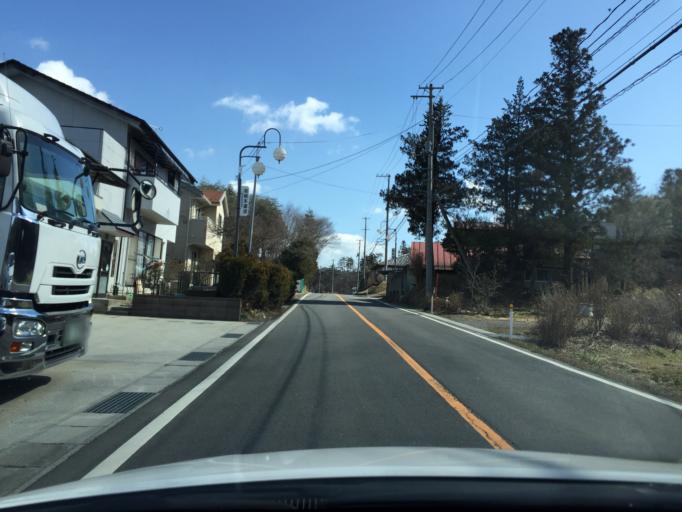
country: JP
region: Fukushima
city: Funehikimachi-funehiki
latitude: 37.3887
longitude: 140.5830
